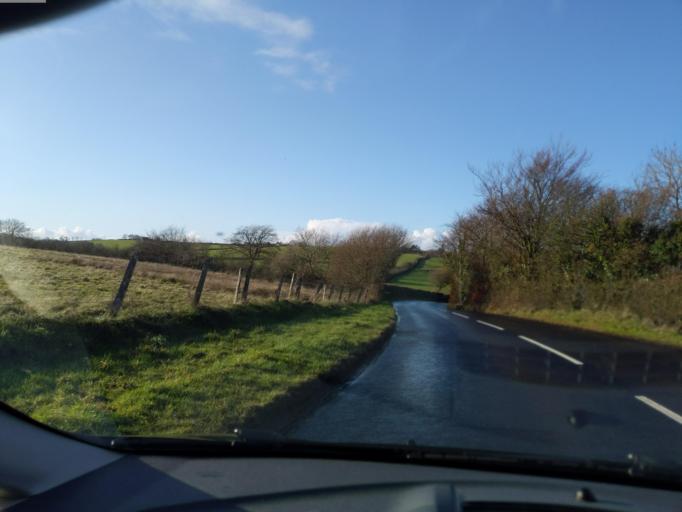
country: GB
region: England
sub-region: Devon
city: Okehampton
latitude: 50.7462
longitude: -4.0173
